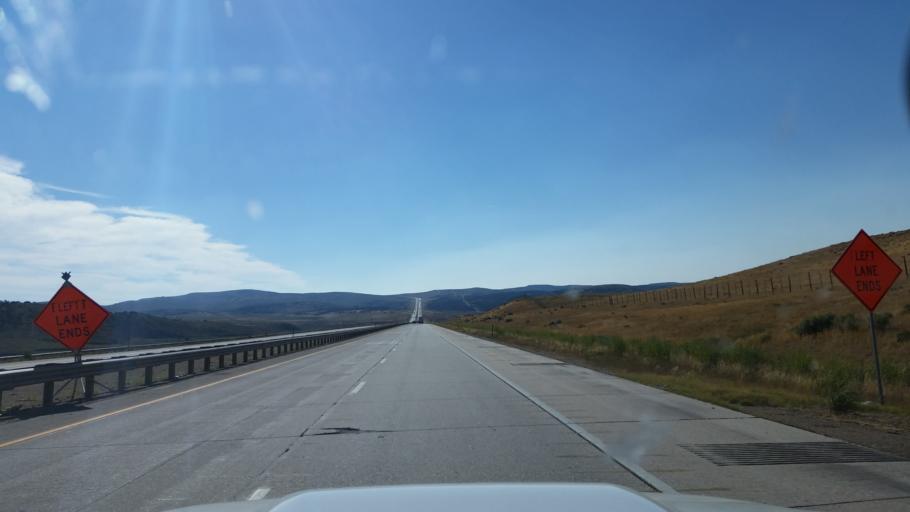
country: US
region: Wyoming
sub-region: Uinta County
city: Mountain View
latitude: 41.2983
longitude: -110.6103
